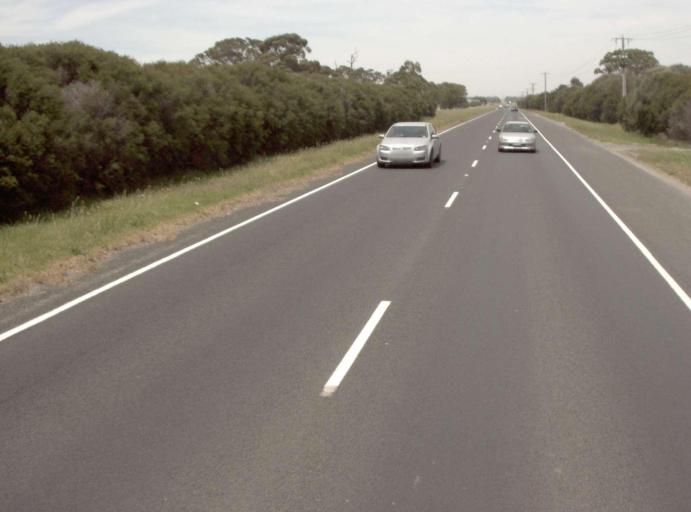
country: AU
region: Victoria
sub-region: Frankston
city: Skye
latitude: -38.0956
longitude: 145.2358
